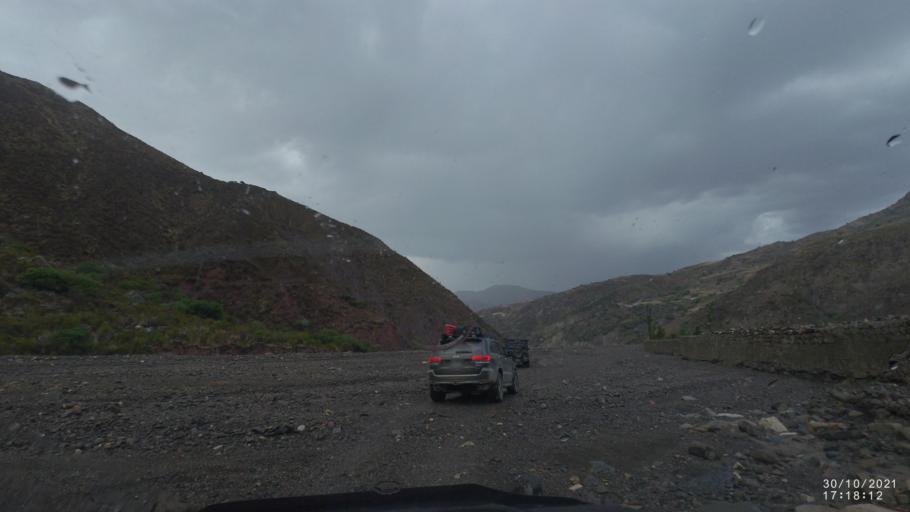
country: BO
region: Cochabamba
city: Colchani
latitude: -17.5365
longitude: -66.6233
